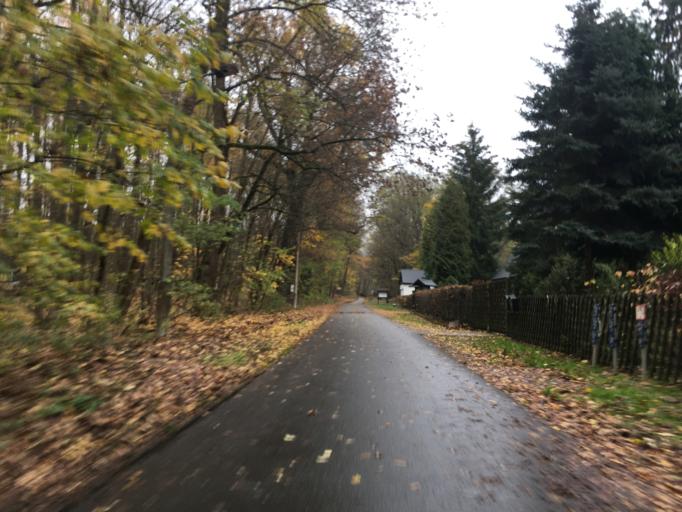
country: DE
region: Brandenburg
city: Gross Lindow
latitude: 52.2844
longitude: 14.5137
